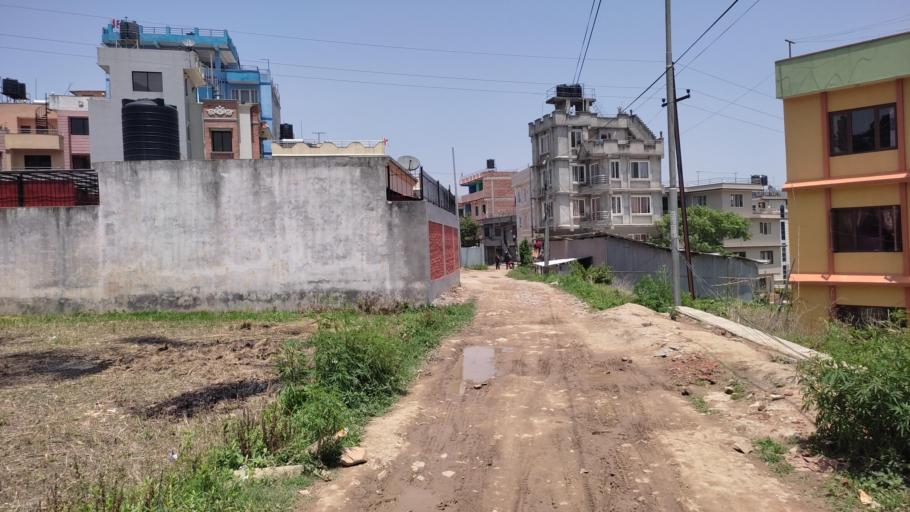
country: NP
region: Central Region
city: Kirtipur
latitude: 27.6720
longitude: 85.2761
